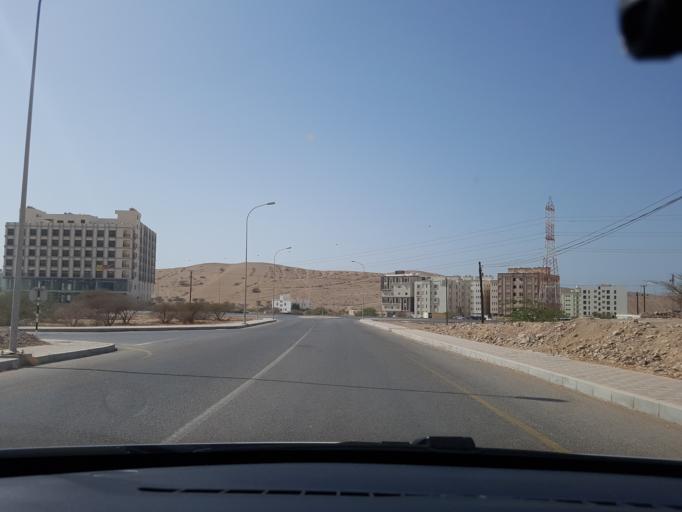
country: OM
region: Muhafazat Masqat
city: Bawshar
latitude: 23.5538
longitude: 58.4092
